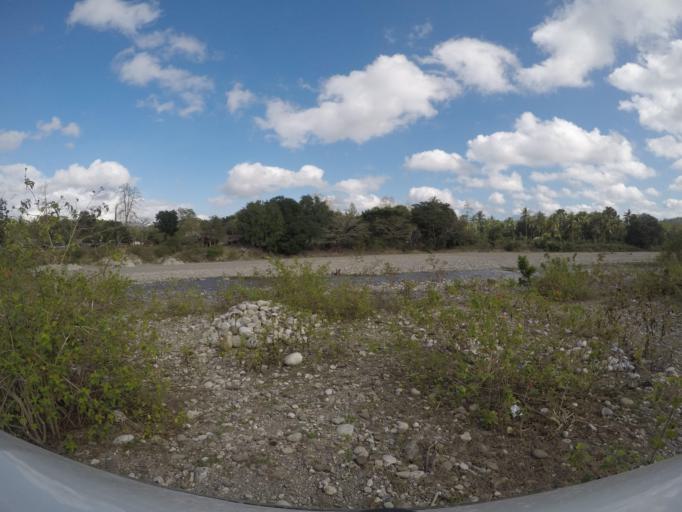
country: TL
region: Viqueque
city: Viqueque
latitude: -8.8794
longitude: 126.3701
